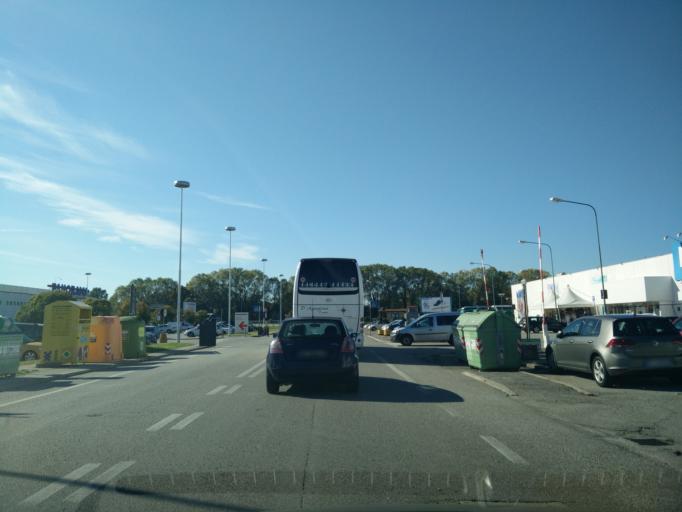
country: IT
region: Veneto
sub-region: Provincia di Venezia
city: Mestre
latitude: 45.4680
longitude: 12.2147
